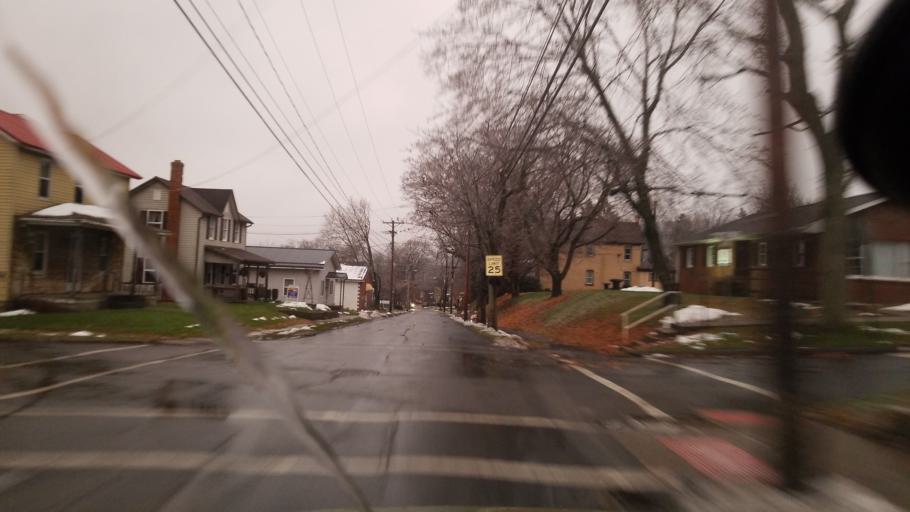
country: US
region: Pennsylvania
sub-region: Clearfield County
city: Clearfield
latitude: 41.0319
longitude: -78.4497
